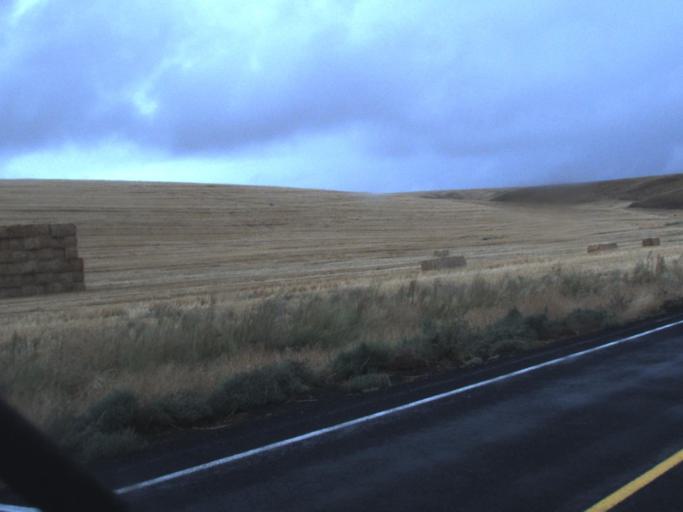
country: US
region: Washington
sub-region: Spokane County
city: Cheney
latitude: 47.1453
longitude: -117.8354
